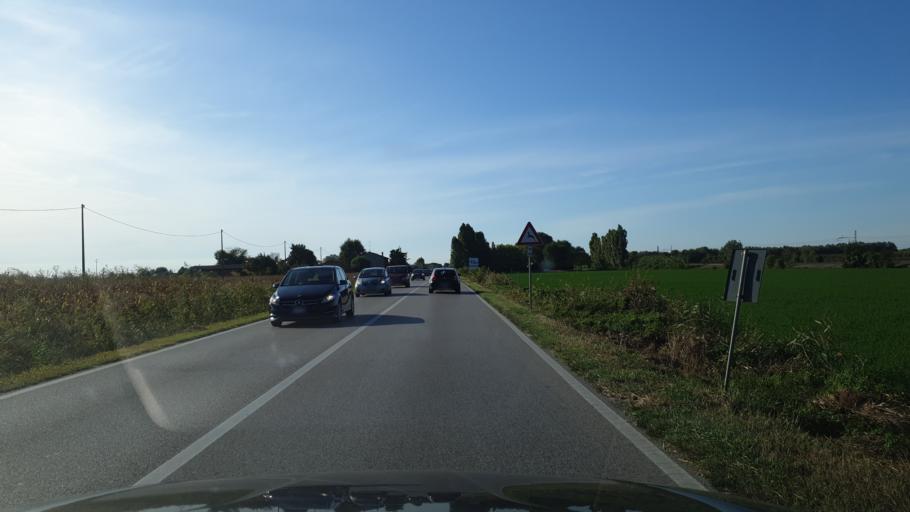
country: IT
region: Emilia-Romagna
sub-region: Provincia di Ravenna
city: Fornace Zarattini
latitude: 44.4502
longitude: 12.1191
